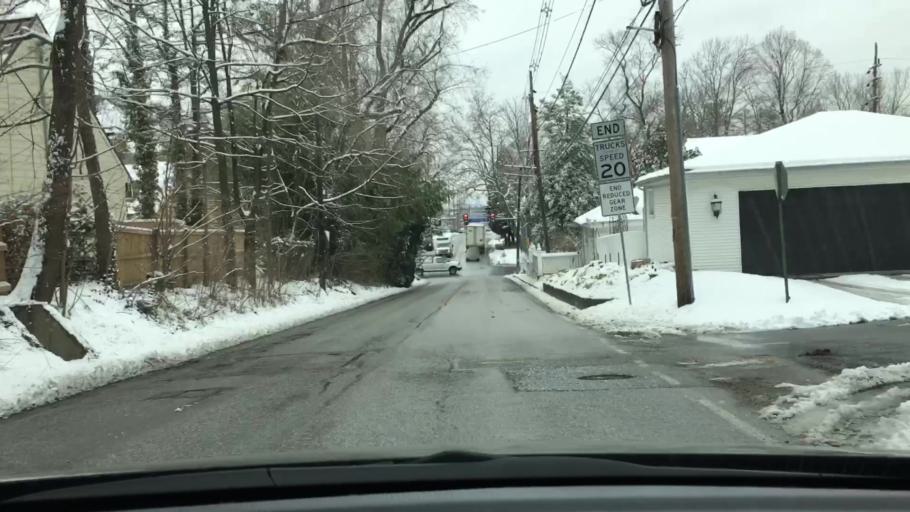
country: US
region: Pennsylvania
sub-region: York County
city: Grantley
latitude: 39.9434
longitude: -76.7328
